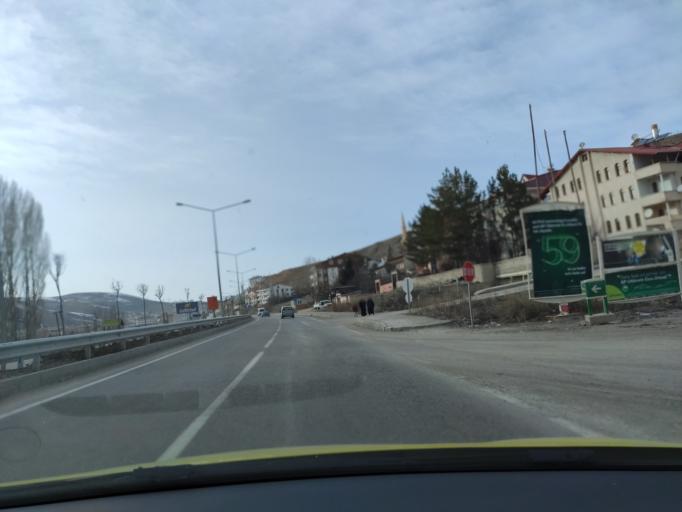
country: TR
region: Bayburt
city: Bayburt
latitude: 40.2423
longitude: 40.2442
